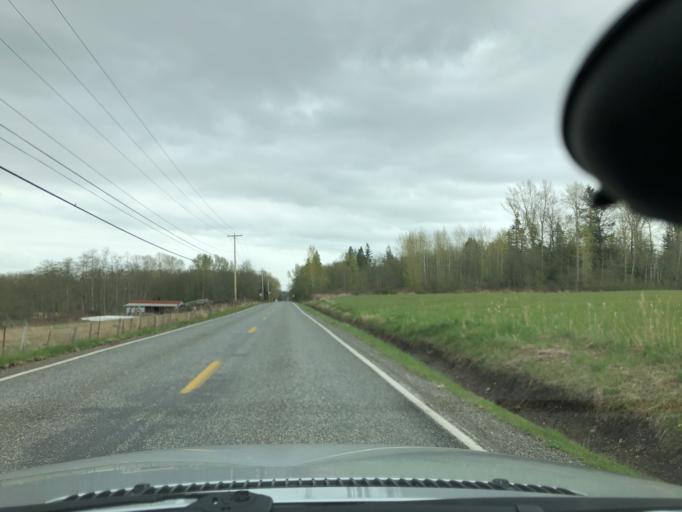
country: US
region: Washington
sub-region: Whatcom County
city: Birch Bay
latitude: 48.8925
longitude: -122.7680
